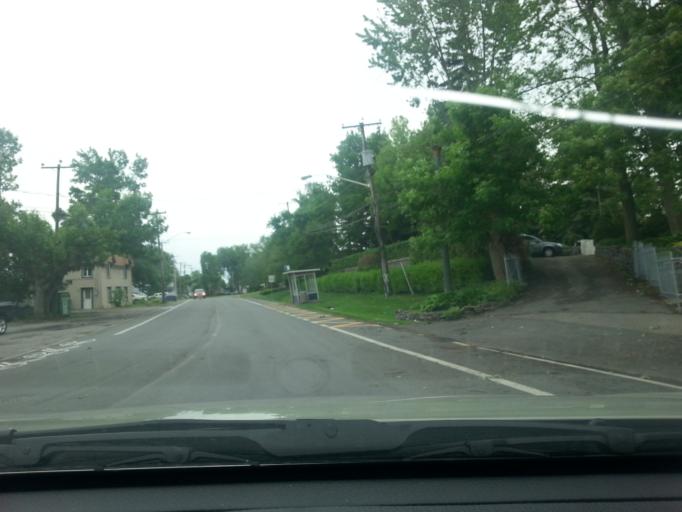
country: CA
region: Quebec
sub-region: Lanaudiere
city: Terrebonne
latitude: 45.6881
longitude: -73.6287
